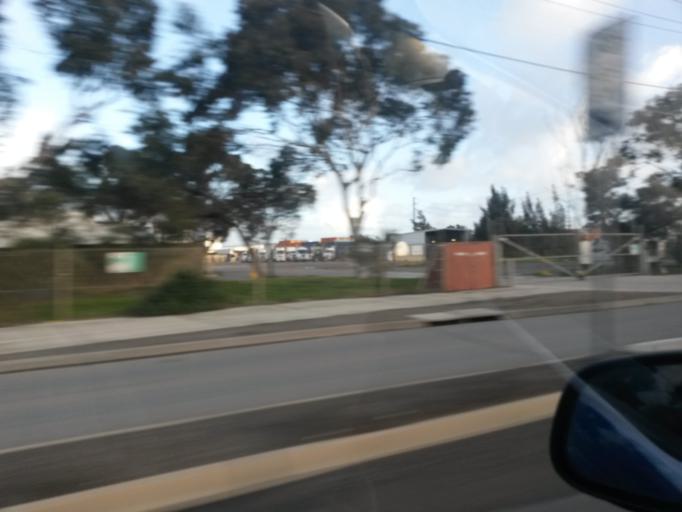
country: AU
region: South Australia
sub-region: Port Adelaide Enfield
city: Alberton
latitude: -34.8396
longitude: 138.5196
